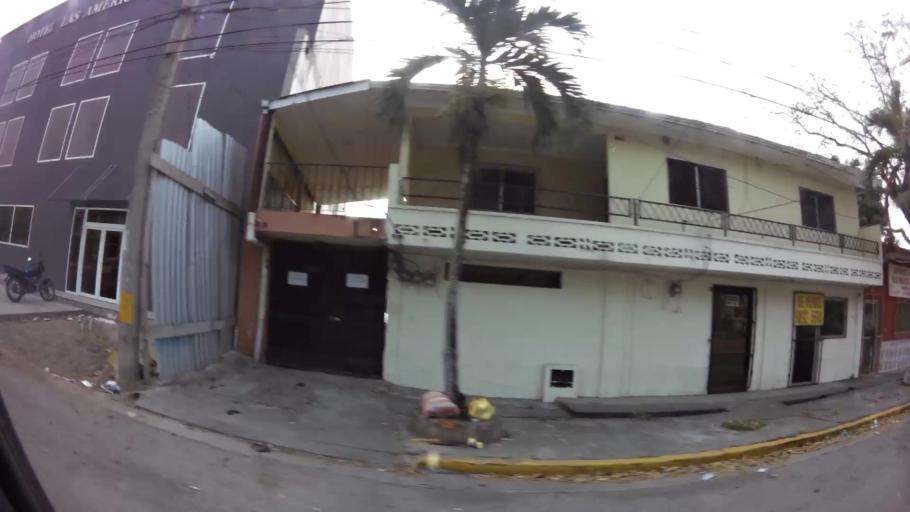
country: HN
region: Cortes
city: San Pedro Sula
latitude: 15.5008
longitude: -88.0356
